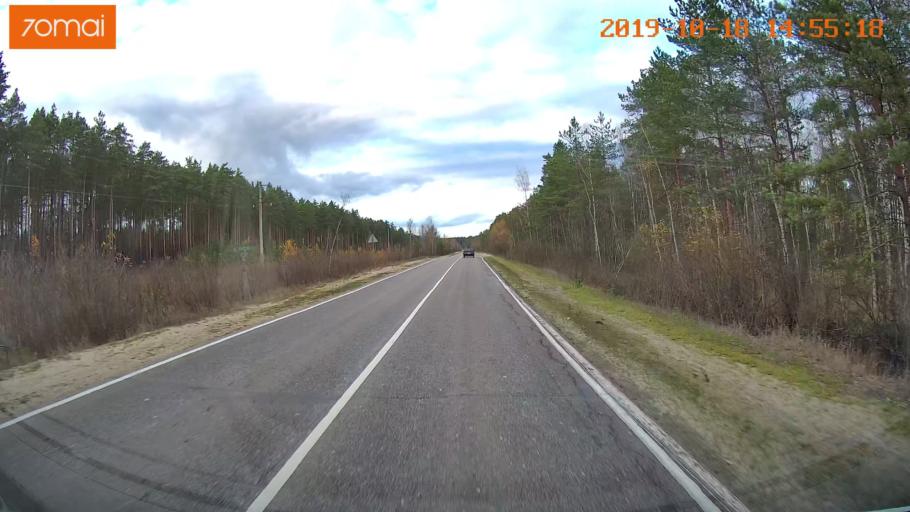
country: RU
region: Vladimir
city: Kurlovo
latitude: 55.4501
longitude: 40.5885
